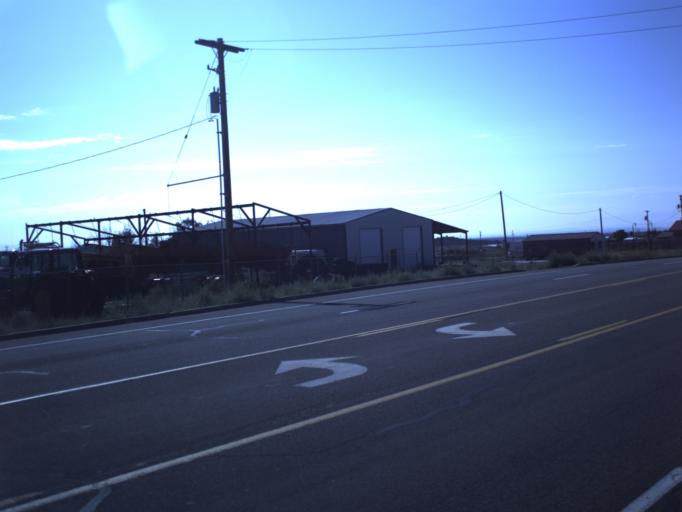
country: US
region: Utah
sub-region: San Juan County
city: Blanding
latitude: 37.6098
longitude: -109.4790
